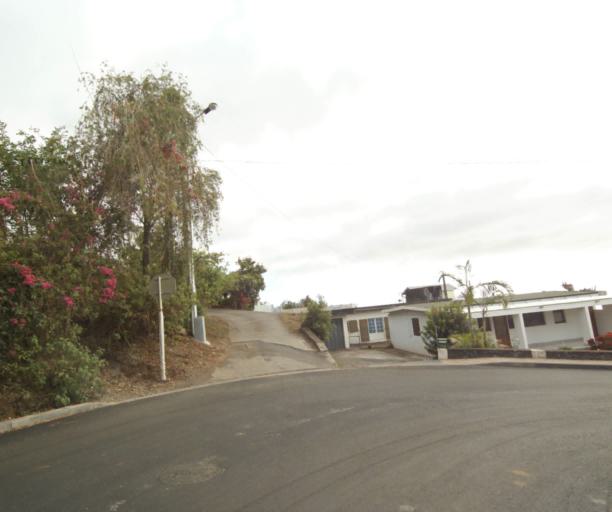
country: RE
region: Reunion
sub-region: Reunion
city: Saint-Paul
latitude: -21.0411
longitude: 55.3016
